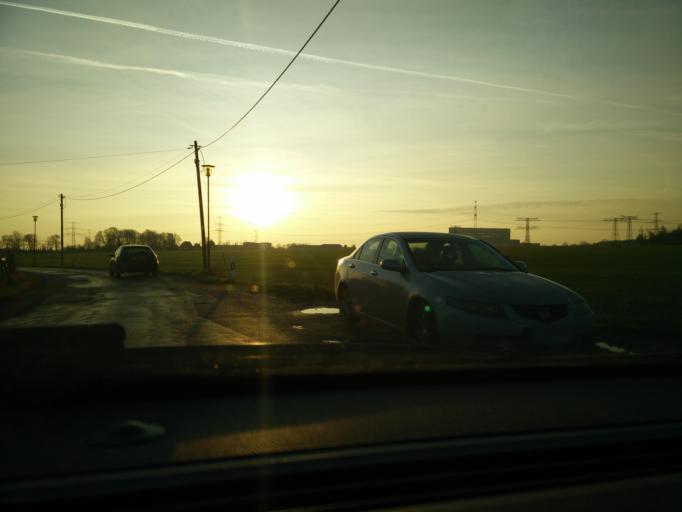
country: DE
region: Saxony
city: Kitzscher
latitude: 51.1750
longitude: 12.5291
